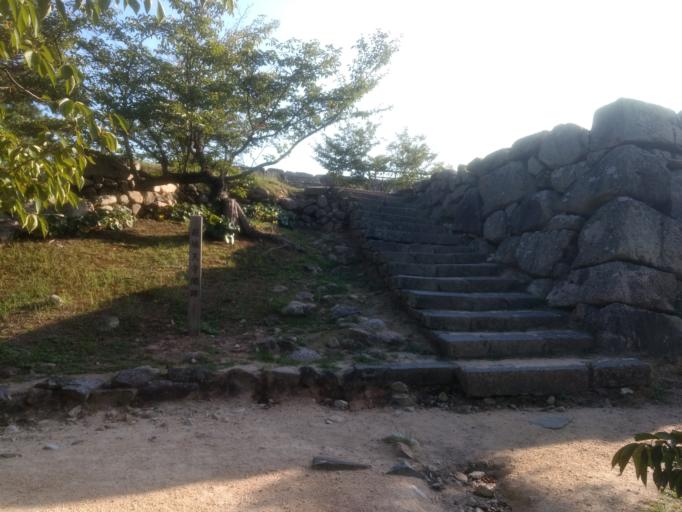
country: JP
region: Yamaguchi
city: Hagi
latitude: 34.4180
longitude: 131.3826
